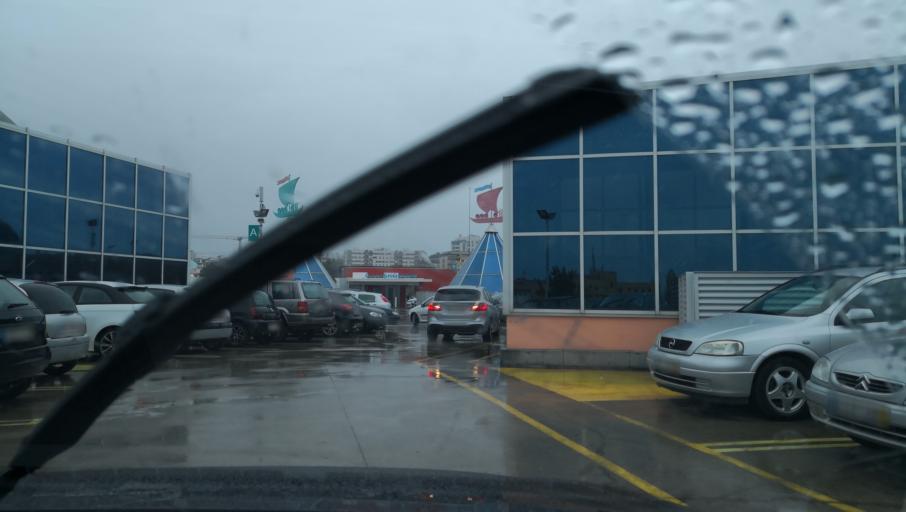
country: PT
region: Porto
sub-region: Vila Nova de Gaia
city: Vila Nova de Gaia
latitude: 41.1179
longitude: -8.6231
